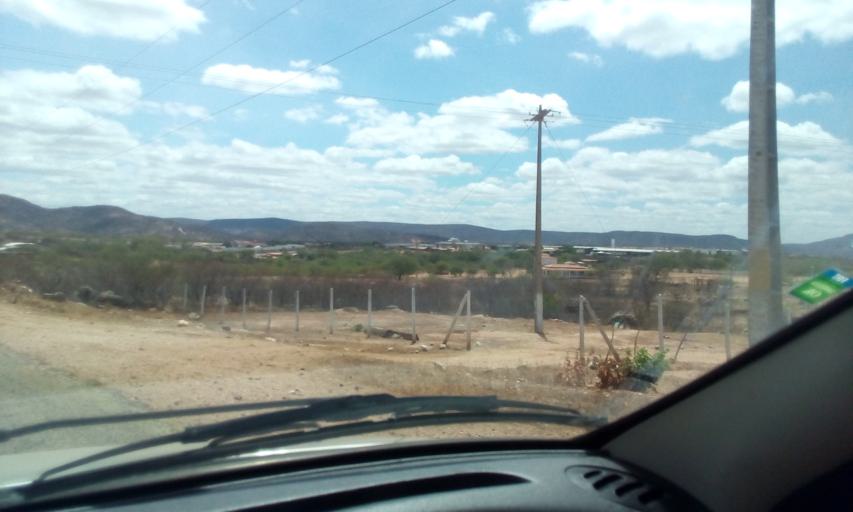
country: BR
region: Rio Grande do Norte
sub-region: Currais Novos
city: Currais Novos
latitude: -6.2777
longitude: -36.5265
